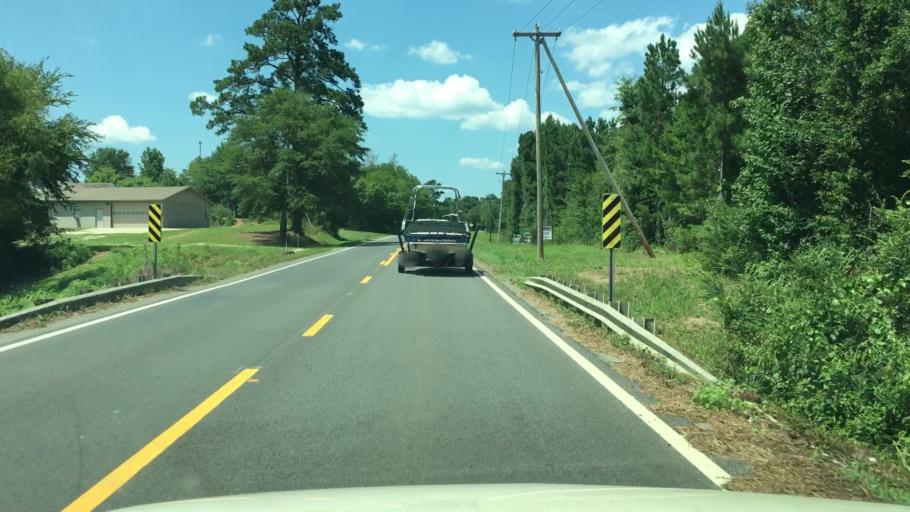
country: US
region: Arkansas
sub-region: Garland County
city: Lake Hamilton
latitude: 34.2971
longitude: -93.1633
